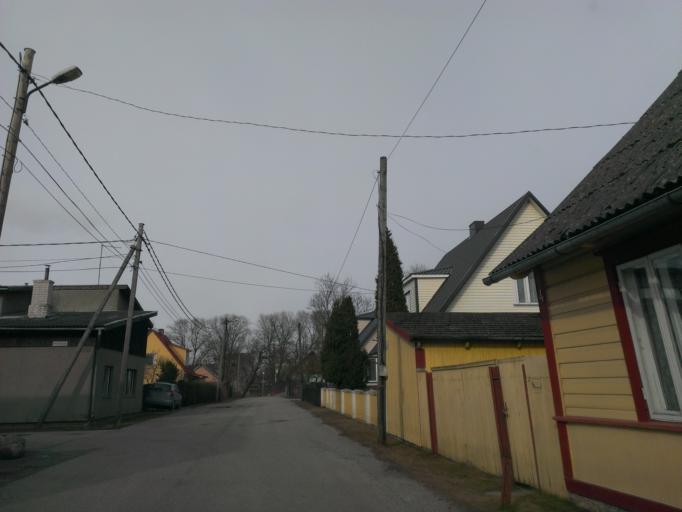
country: EE
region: Paernumaa
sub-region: Paernu linn
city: Parnu
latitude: 58.3912
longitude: 24.4700
